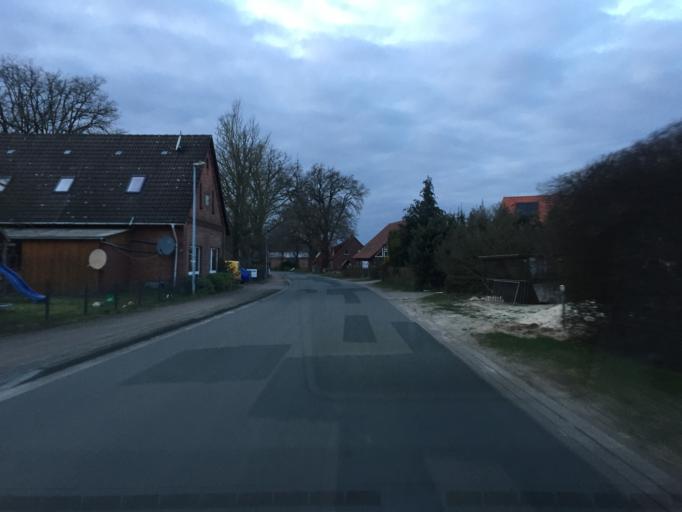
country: DE
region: Lower Saxony
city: Steimbke
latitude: 52.5932
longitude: 9.4001
